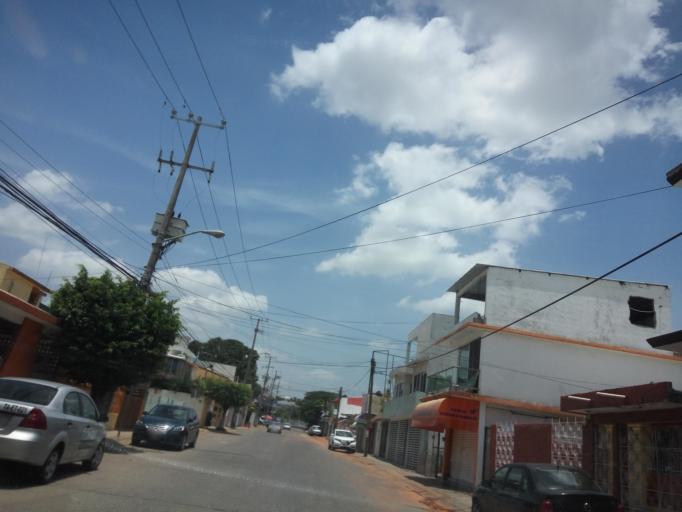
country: MX
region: Tabasco
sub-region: Nacajuca
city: Bosque de Saloya
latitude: 18.0059
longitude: -92.9423
